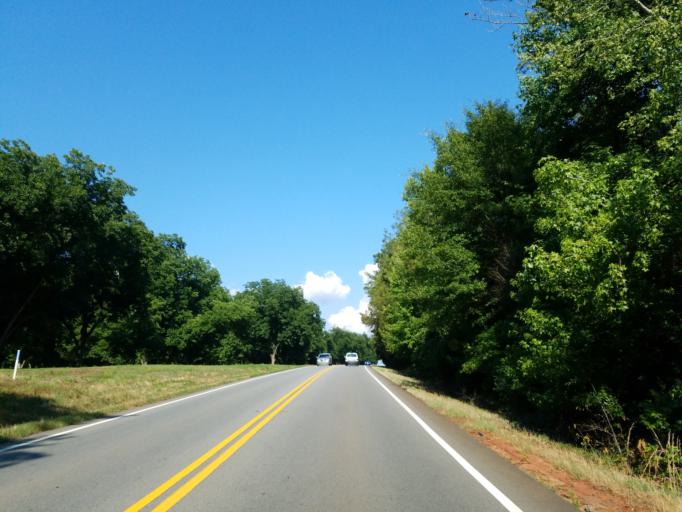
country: US
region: Georgia
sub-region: Peach County
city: Fort Valley
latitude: 32.5568
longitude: -83.8374
